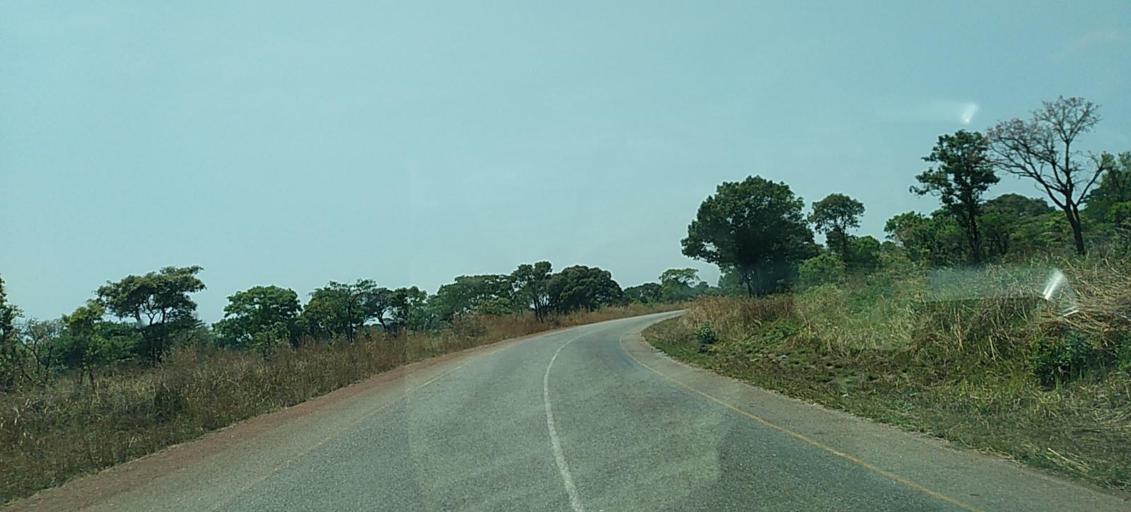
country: ZM
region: North-Western
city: Solwezi
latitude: -12.3795
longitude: 26.1890
